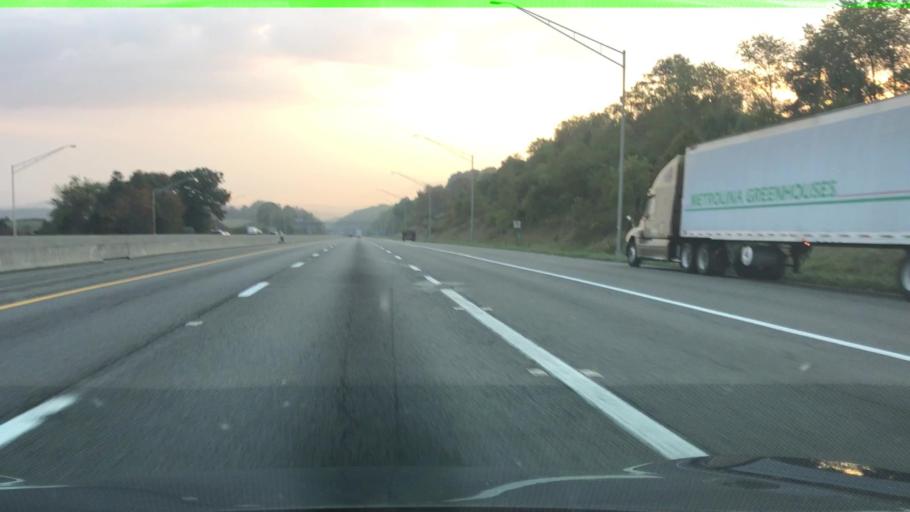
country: US
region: Virginia
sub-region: Montgomery County
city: Christiansburg
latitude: 37.1439
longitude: -80.3479
